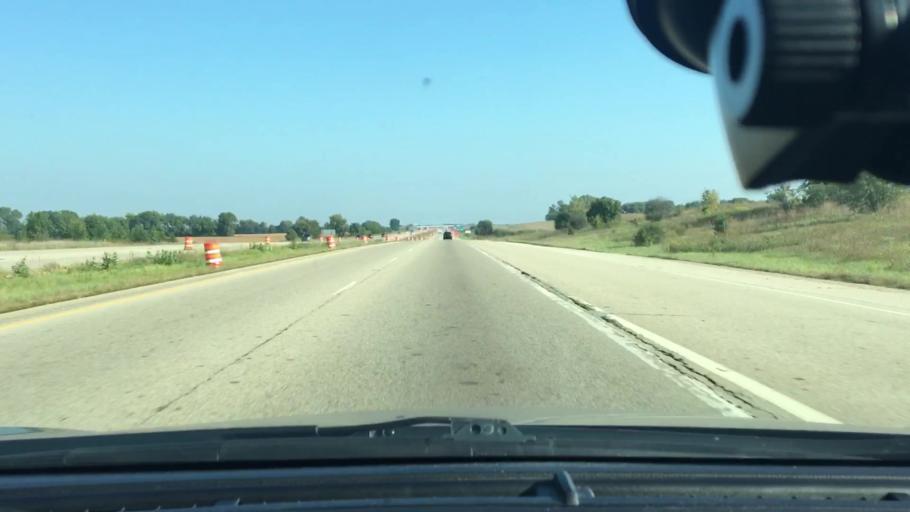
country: US
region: Wisconsin
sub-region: Rock County
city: Beloit
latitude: 42.5313
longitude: -88.9750
